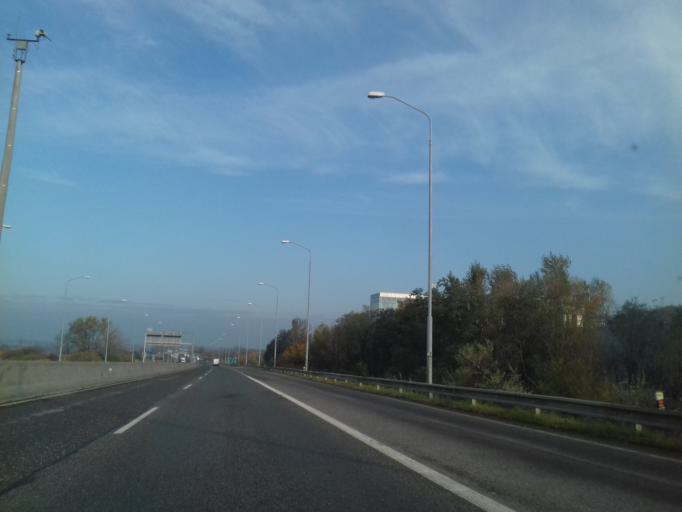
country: SK
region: Bratislavsky
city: Stupava
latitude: 48.2059
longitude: 17.0396
